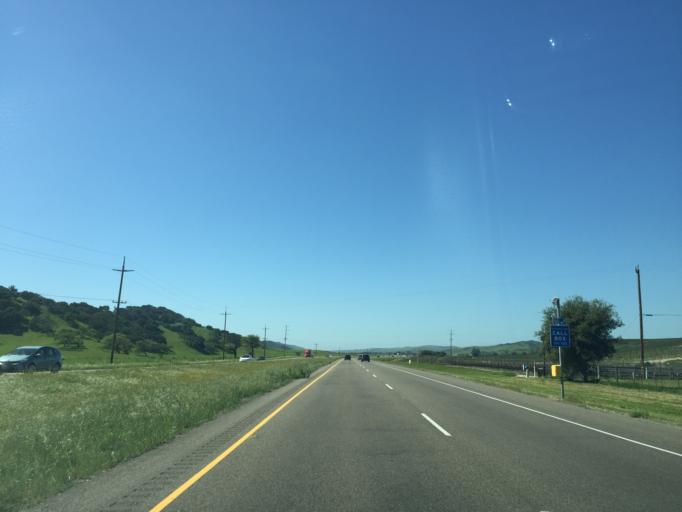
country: US
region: California
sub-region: Santa Barbara County
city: Los Alamos
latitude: 34.7267
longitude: -120.2230
